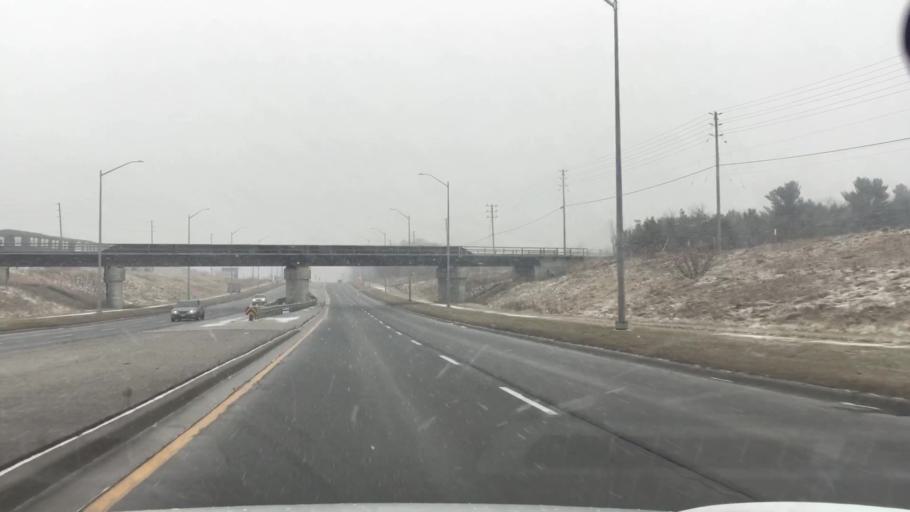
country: CA
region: Ontario
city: Pickering
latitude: 43.8840
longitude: -79.0896
